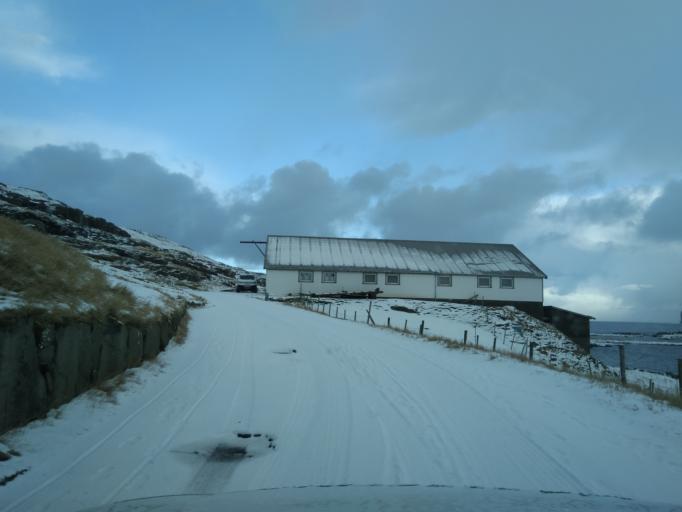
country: FO
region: Eysturoy
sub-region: Eidi
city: Eidi
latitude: 62.3040
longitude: -7.0910
